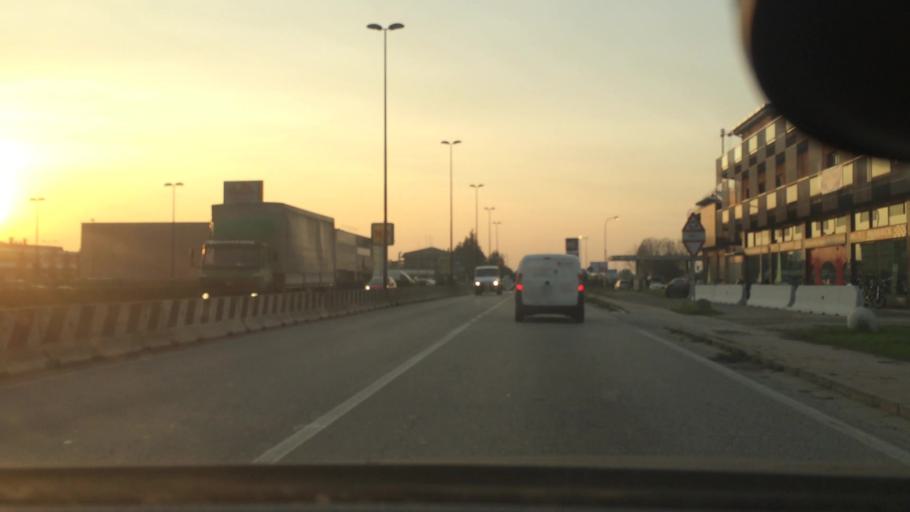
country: IT
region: Lombardy
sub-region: Citta metropolitana di Milano
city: Solaro
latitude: 45.6176
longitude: 9.0660
